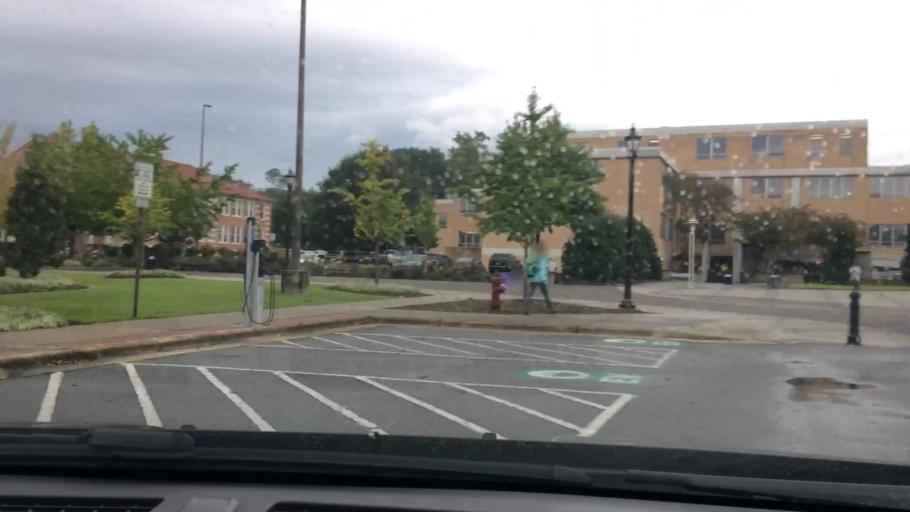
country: US
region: North Carolina
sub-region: Pitt County
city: Greenville
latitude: 35.6056
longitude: -77.3623
